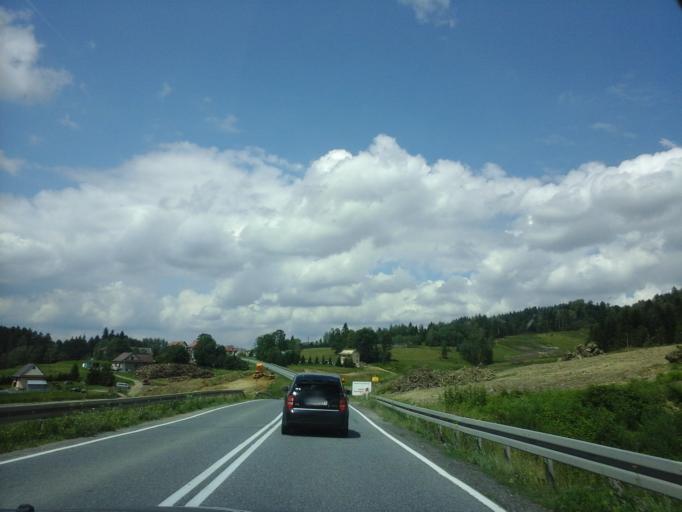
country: PL
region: Lesser Poland Voivodeship
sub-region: Powiat suski
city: Naprawa
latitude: 49.6464
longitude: 19.9083
